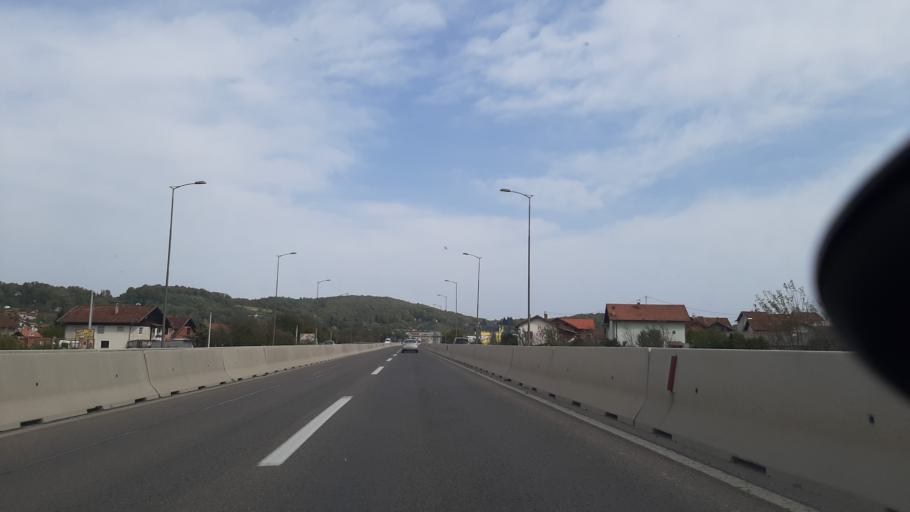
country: BA
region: Republika Srpska
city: Trn
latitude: 44.8641
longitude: 17.2465
